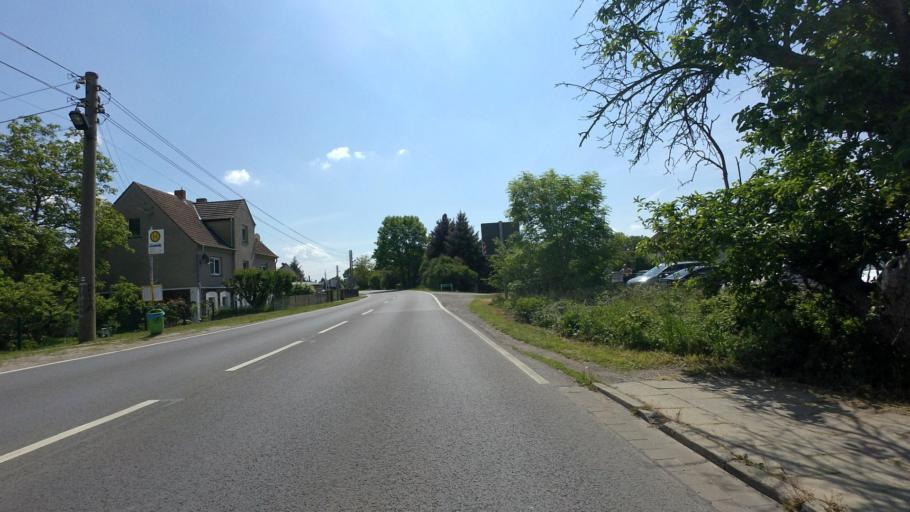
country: DE
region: Brandenburg
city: Luebben
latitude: 51.9424
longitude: 13.9143
